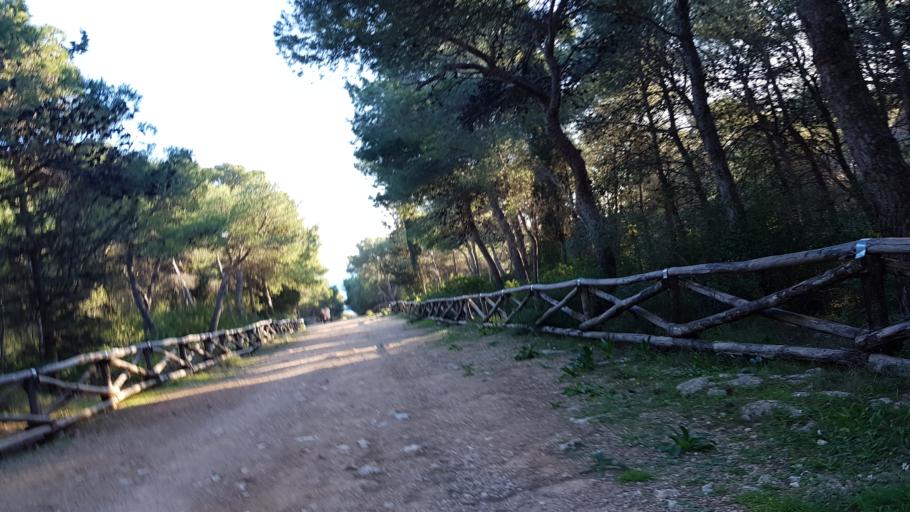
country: IT
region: Apulia
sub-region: Provincia di Lecce
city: Nardo
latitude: 40.1506
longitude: 17.9715
